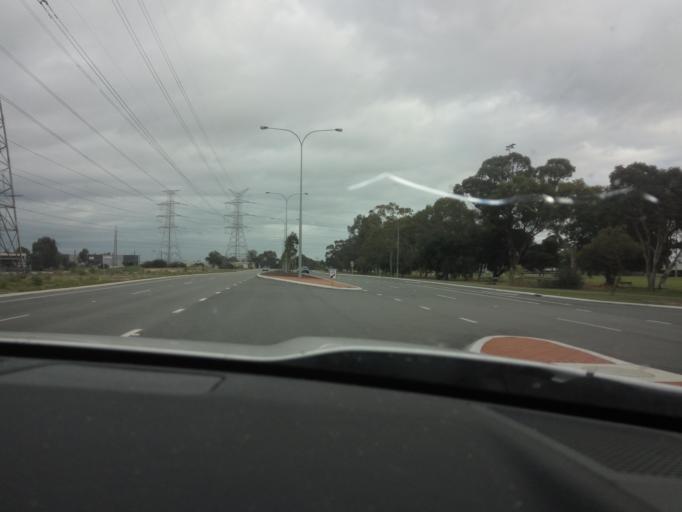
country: AU
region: Western Australia
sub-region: City of Cockburn
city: South Lake
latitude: -32.1194
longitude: 115.8440
